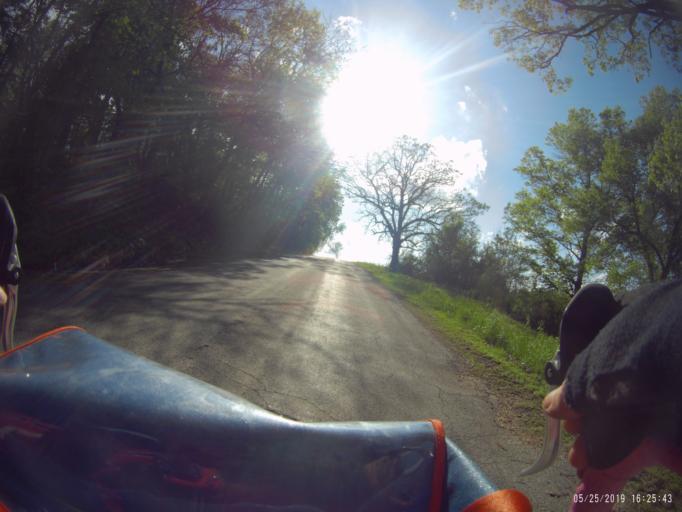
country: US
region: Wisconsin
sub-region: Dane County
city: Mount Horeb
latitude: 42.9510
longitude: -89.7029
